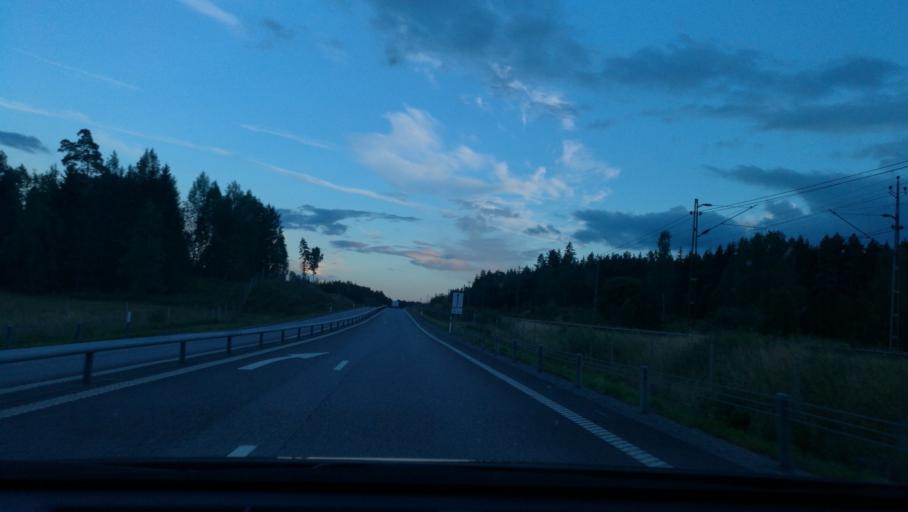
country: SE
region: Soedermanland
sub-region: Katrineholms Kommun
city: Katrineholm
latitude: 58.9237
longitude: 16.1959
